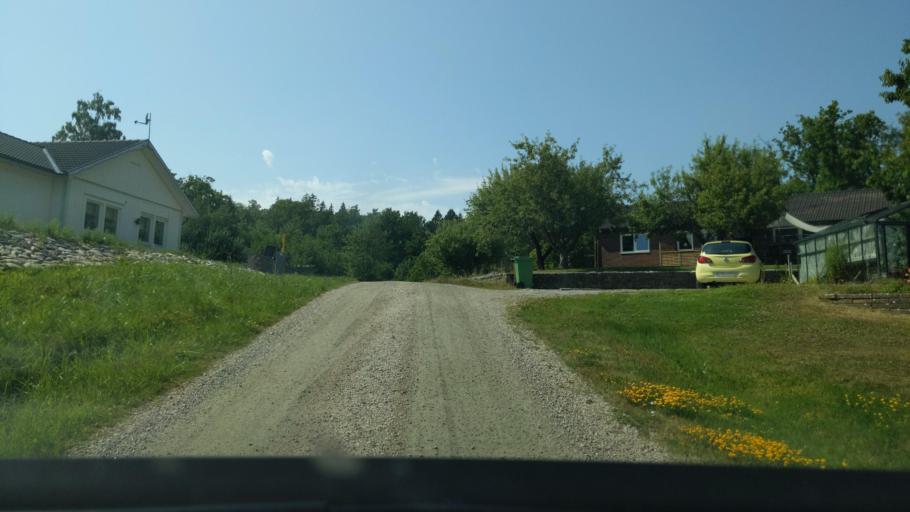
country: SE
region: Vaestra Goetaland
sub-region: Uddevalla Kommun
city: Uddevalla
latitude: 58.3362
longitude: 11.7983
